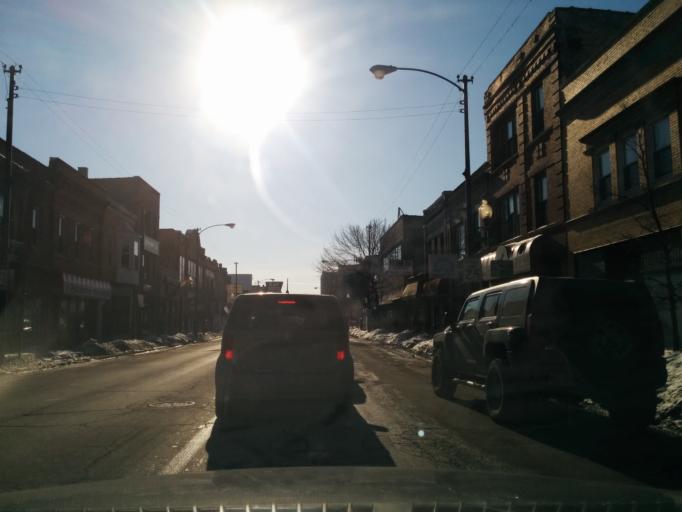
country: US
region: Illinois
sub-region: Cook County
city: Lincolnwood
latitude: 41.9340
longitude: -87.7154
